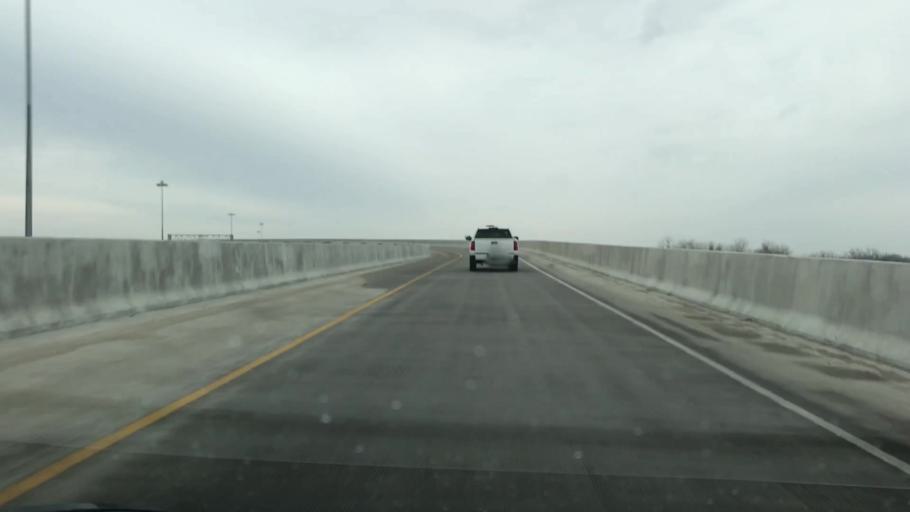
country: US
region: Iowa
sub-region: Pottawattamie County
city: Council Bluffs
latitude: 41.2323
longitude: -95.8357
